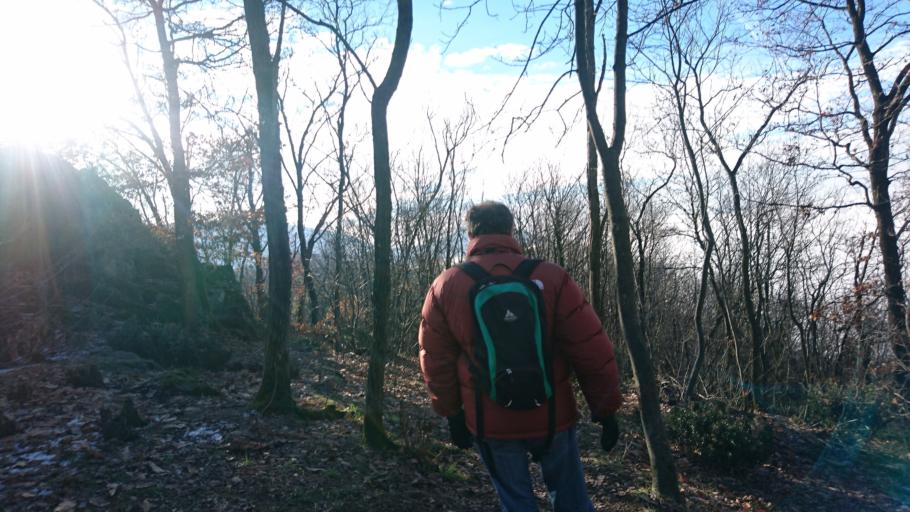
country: IT
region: Veneto
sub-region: Provincia di Padova
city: Treponti
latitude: 45.3368
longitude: 11.6848
